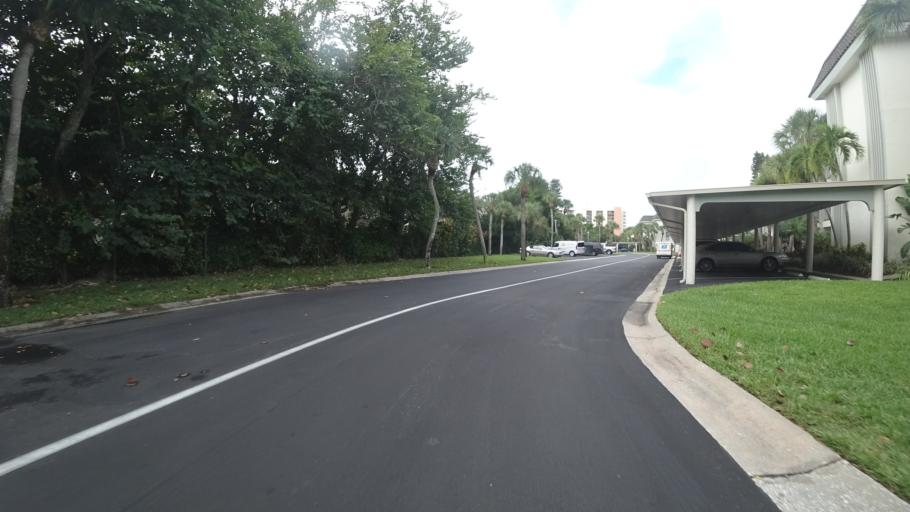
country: US
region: Florida
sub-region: Manatee County
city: Longboat Key
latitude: 27.3948
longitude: -82.6423
